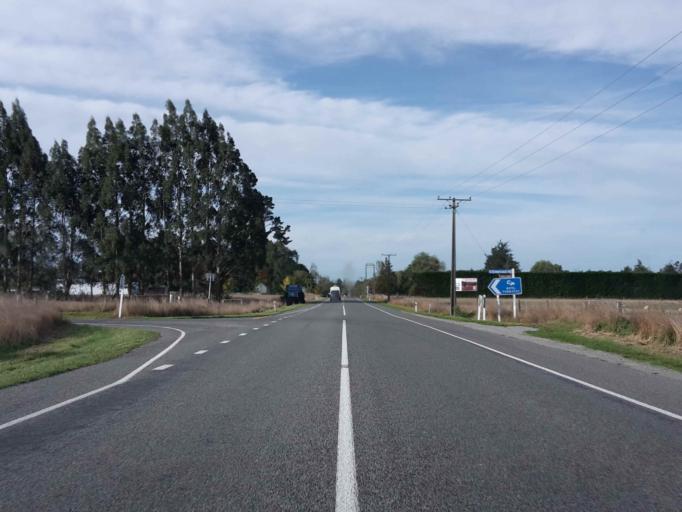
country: NZ
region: Canterbury
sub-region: Timaru District
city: Pleasant Point
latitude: -44.1092
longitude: 171.2322
